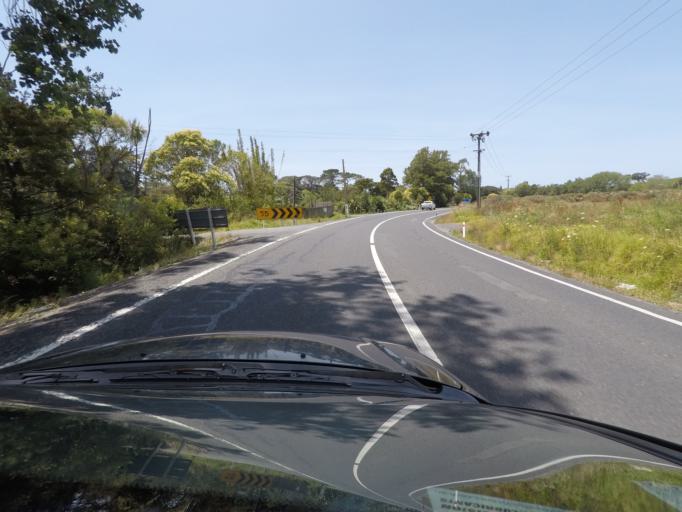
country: NZ
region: Auckland
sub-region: Auckland
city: Warkworth
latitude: -36.3445
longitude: 174.7285
